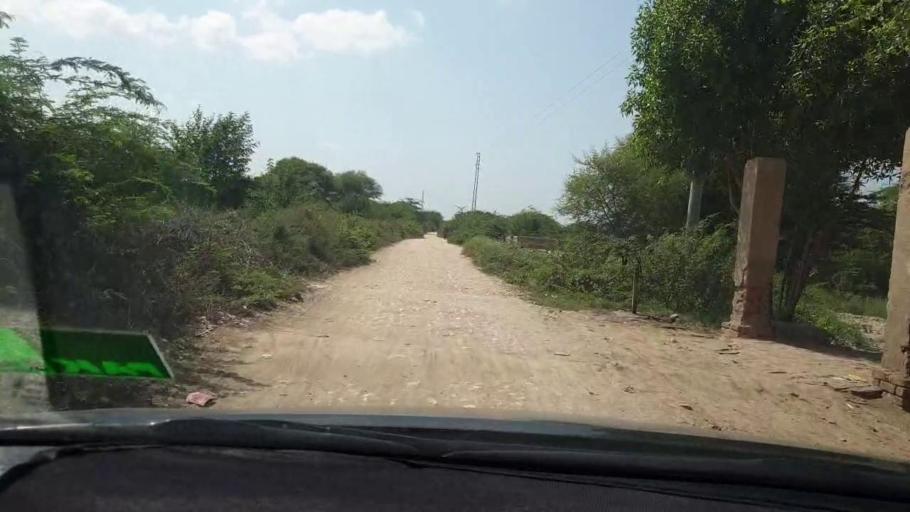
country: PK
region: Sindh
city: Naukot
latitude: 24.9148
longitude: 69.2534
